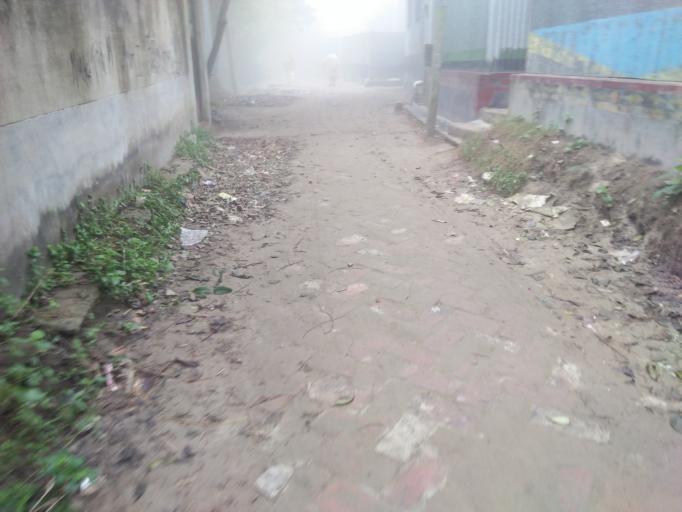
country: BD
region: Dhaka
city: Azimpur
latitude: 23.6882
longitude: 90.3019
